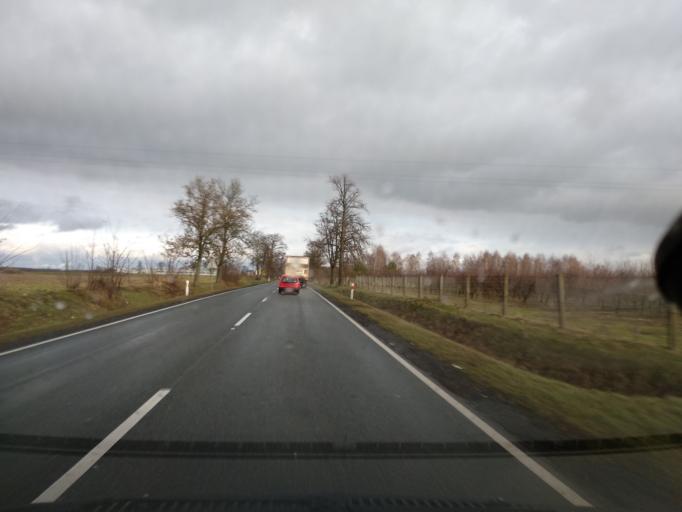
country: PL
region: Greater Poland Voivodeship
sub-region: Powiat koninski
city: Stare Miasto
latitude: 52.1411
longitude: 18.1926
